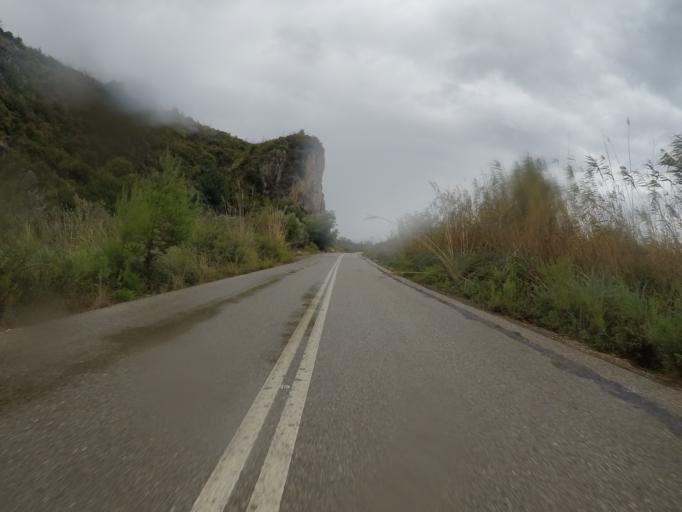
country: GR
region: West Greece
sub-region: Nomos Ileias
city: Zacharo
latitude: 37.5237
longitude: 21.5959
